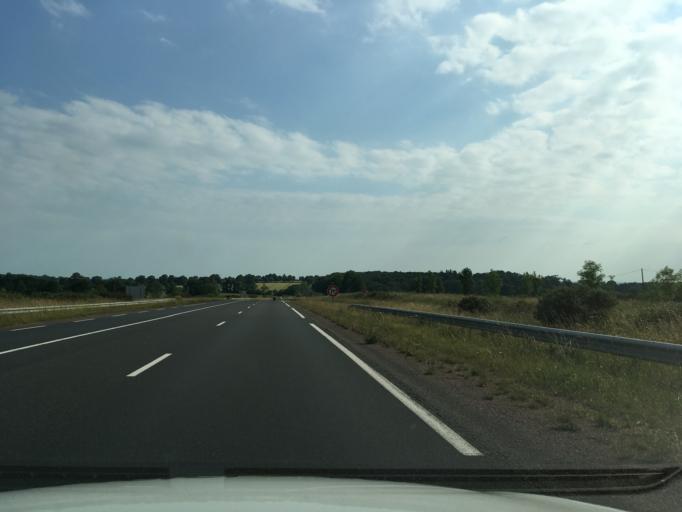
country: FR
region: Poitou-Charentes
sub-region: Departement des Deux-Sevres
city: Saint-Pardoux
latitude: 46.5172
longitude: -0.3295
